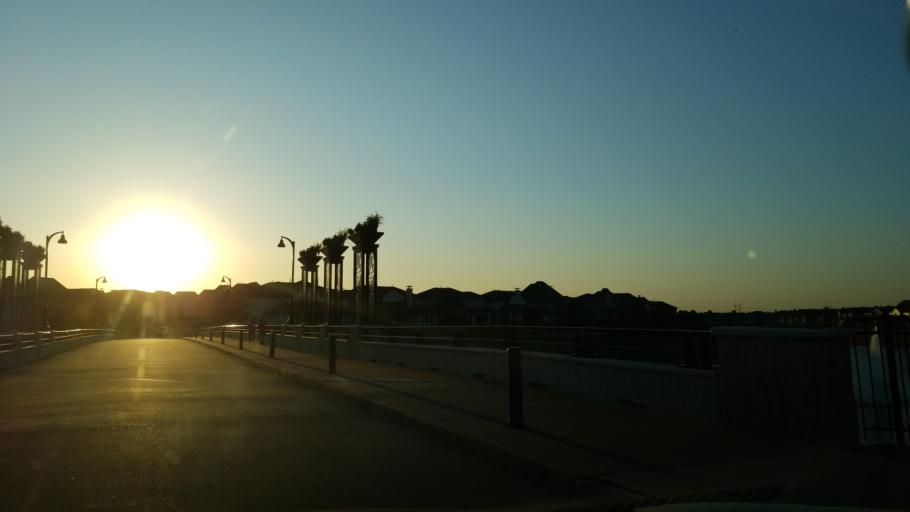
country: US
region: Texas
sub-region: Dallas County
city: Coppell
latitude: 32.9026
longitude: -96.9837
